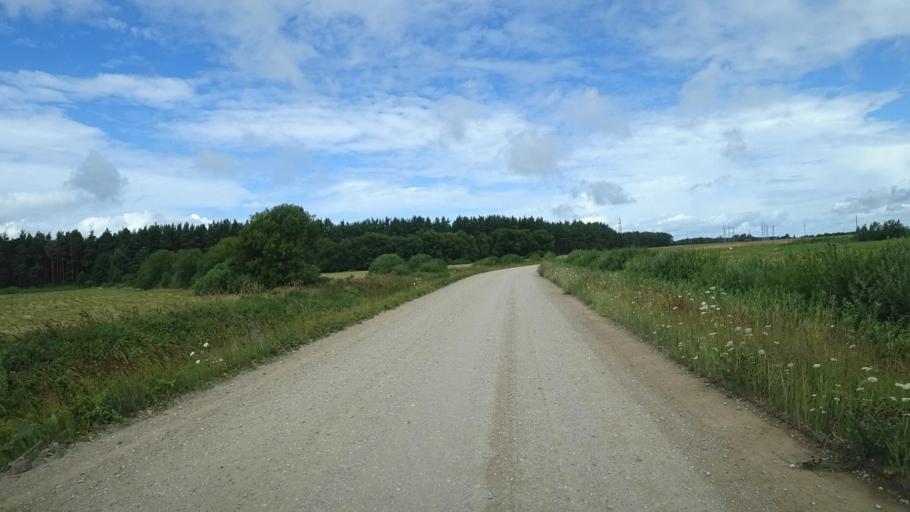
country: LV
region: Liepaja
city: Vec-Liepaja
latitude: 56.6327
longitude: 21.0475
